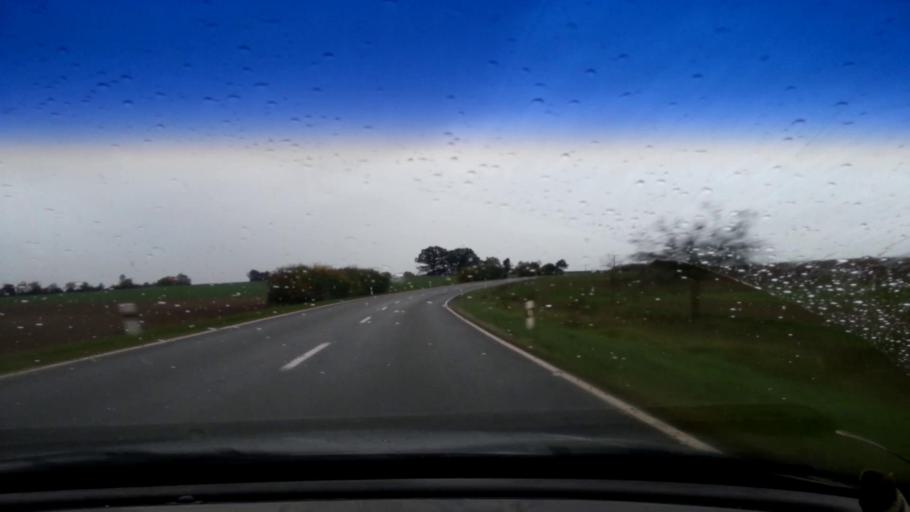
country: DE
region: Bavaria
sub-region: Upper Franconia
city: Burgebrach
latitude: 49.8556
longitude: 10.7253
